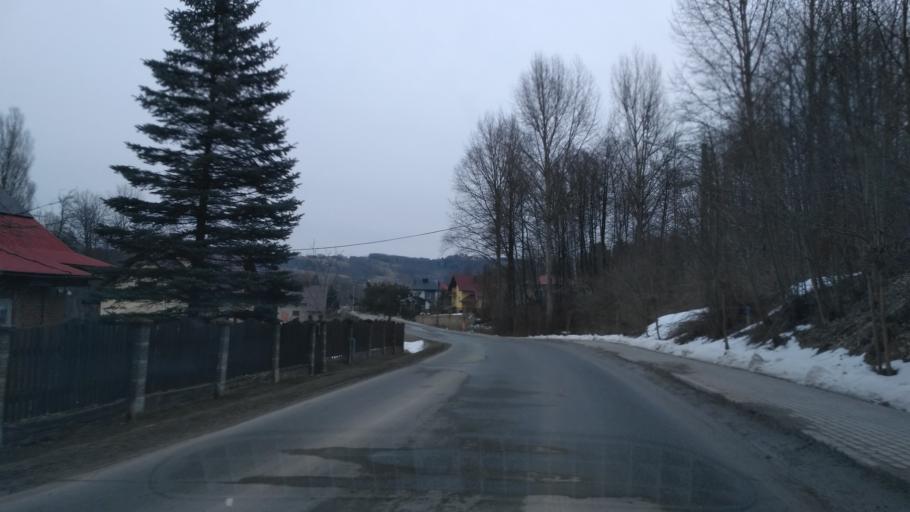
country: PL
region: Subcarpathian Voivodeship
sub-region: Powiat rzeszowski
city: Lubenia
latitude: 49.9239
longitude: 21.9458
